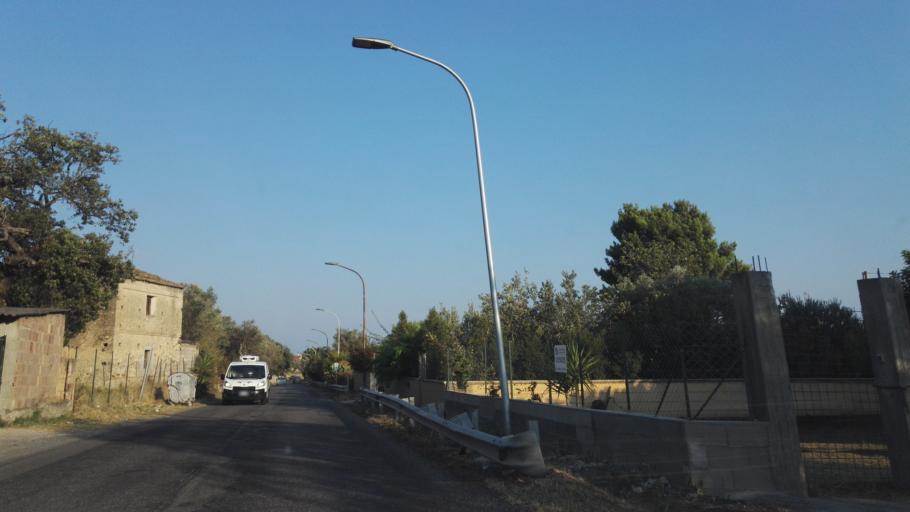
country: IT
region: Calabria
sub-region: Provincia di Reggio Calabria
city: Marina di Gioiosa Ionica
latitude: 38.3086
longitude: 16.3184
